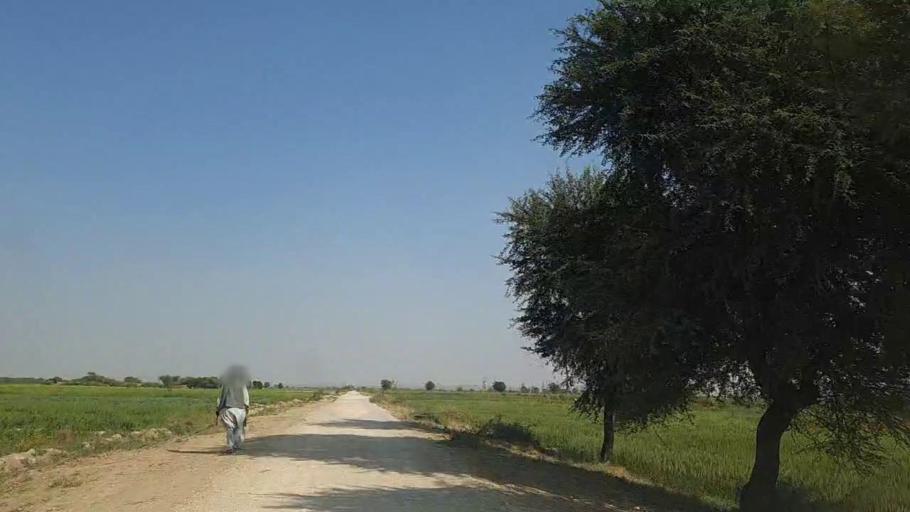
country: PK
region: Sindh
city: Naukot
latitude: 24.8992
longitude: 69.4625
